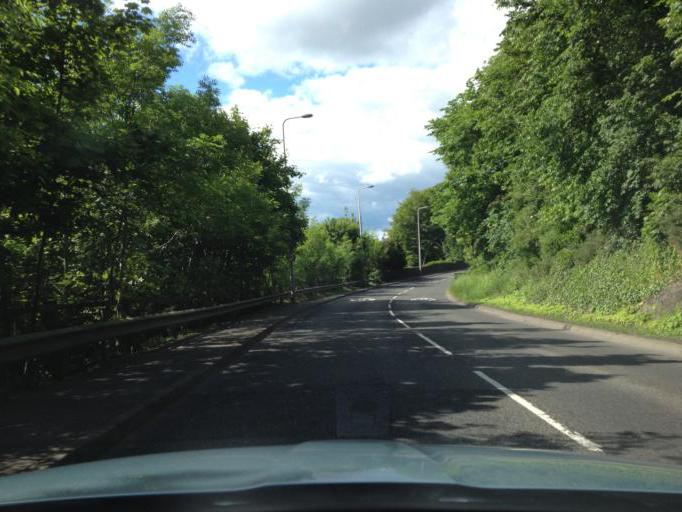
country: GB
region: Scotland
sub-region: Perth and Kinross
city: Perth
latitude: 56.3859
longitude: -3.4194
